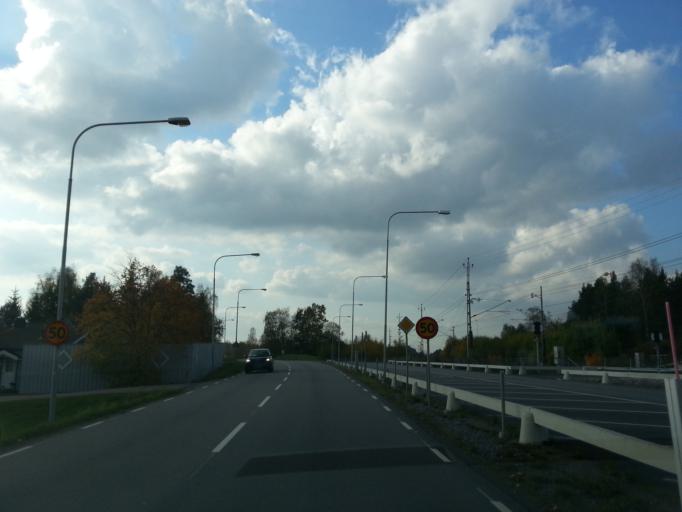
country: SE
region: OEstergoetland
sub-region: Linkopings Kommun
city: Linghem
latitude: 58.4360
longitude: 15.7845
